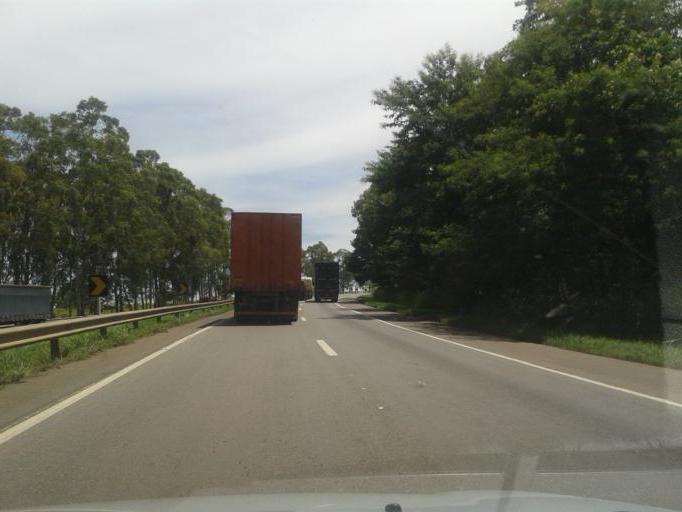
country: BR
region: Goias
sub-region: Hidrolandia
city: Hidrolandia
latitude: -16.9407
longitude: -49.2536
